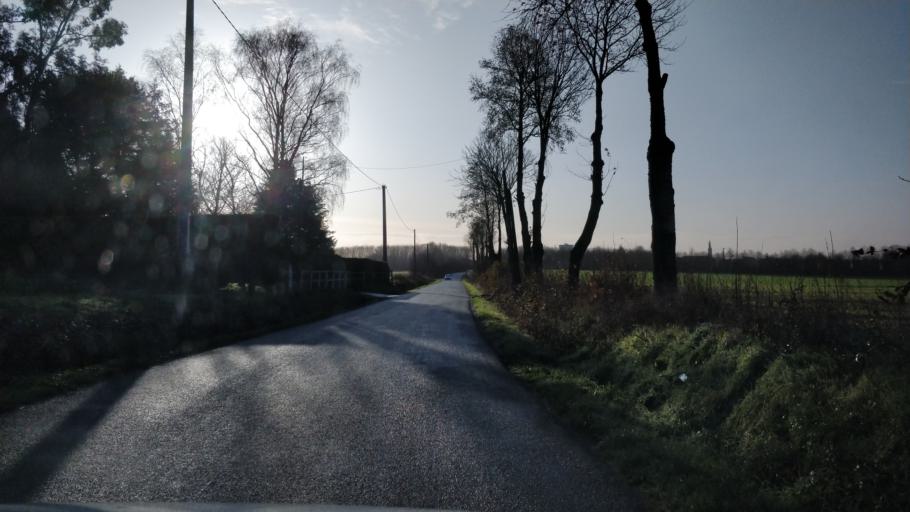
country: FR
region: Brittany
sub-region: Departement d'Ille-et-Vilaine
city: Chavagne
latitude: 48.0630
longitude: -1.7899
